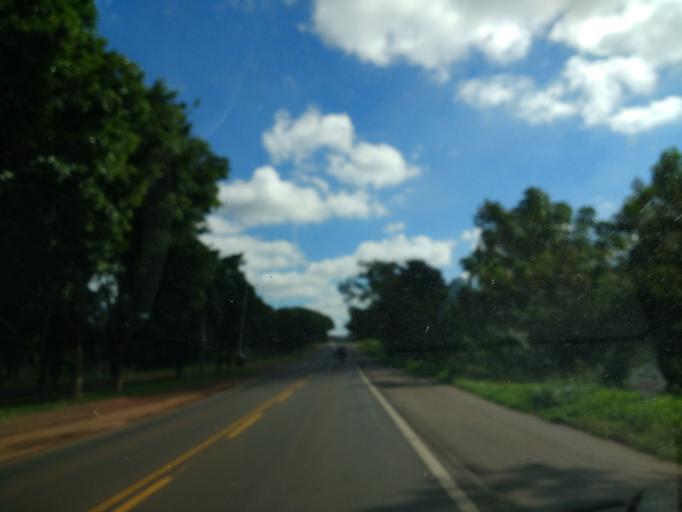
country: BR
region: Parana
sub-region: Alto Piquiri
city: Alto Piquiri
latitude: -23.8925
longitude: -53.4470
